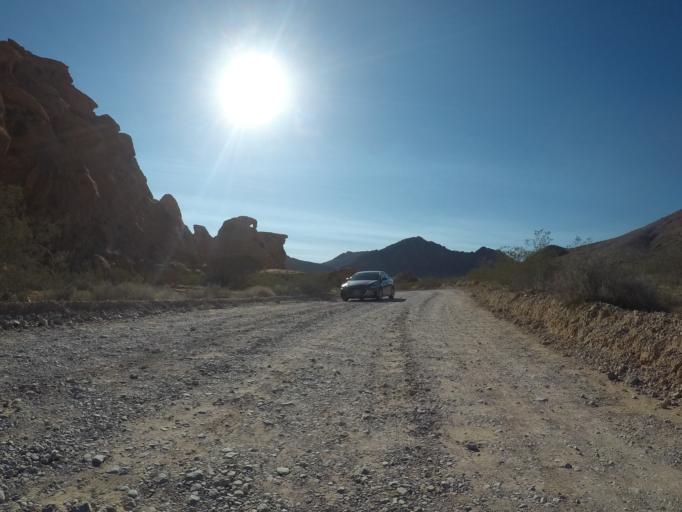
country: US
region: Nevada
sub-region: Clark County
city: Moapa Valley
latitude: 36.4171
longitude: -114.5600
